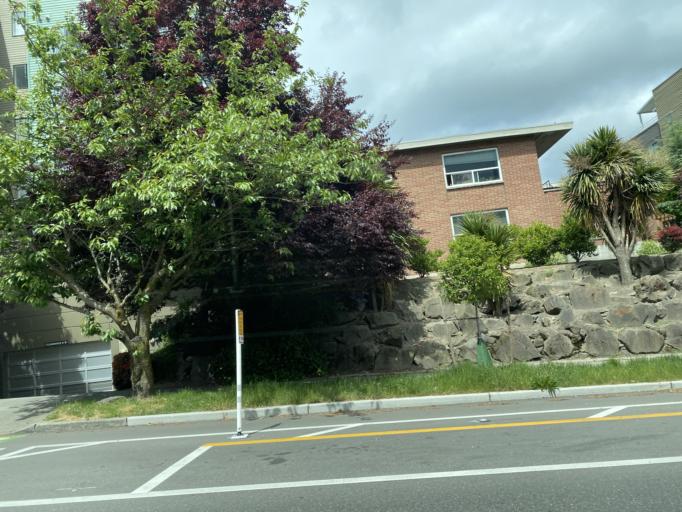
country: US
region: Washington
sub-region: King County
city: White Center
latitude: 47.5641
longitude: -122.3746
